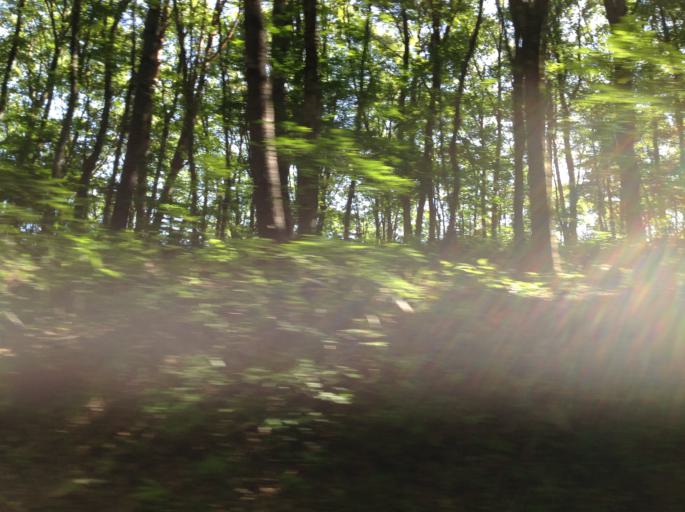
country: JP
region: Akita
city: Kakunodatemachi
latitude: 39.6982
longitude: 140.6624
